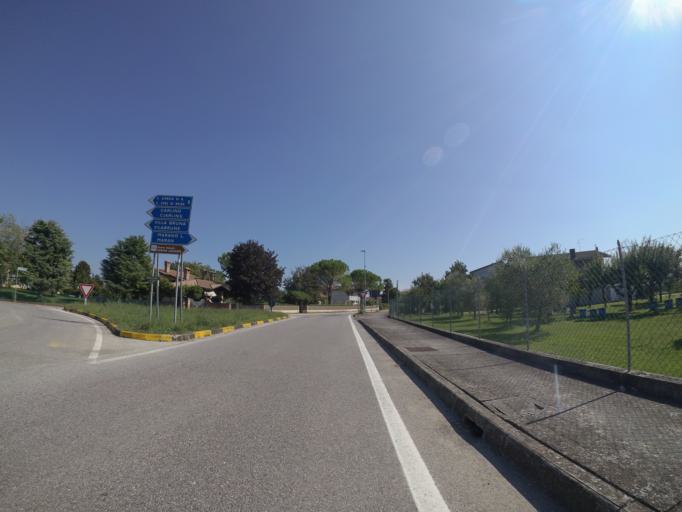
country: IT
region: Friuli Venezia Giulia
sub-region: Provincia di Udine
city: Marano Lagunare
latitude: 45.7730
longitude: 13.1668
